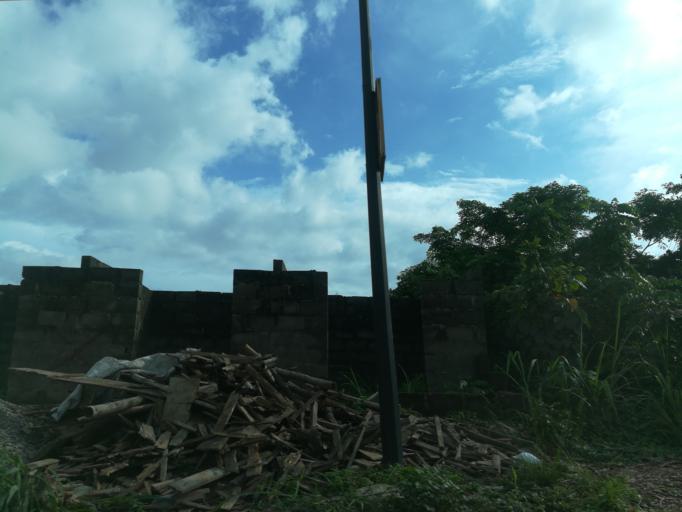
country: NG
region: Lagos
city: Ebute Ikorodu
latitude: 6.5970
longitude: 3.5010
